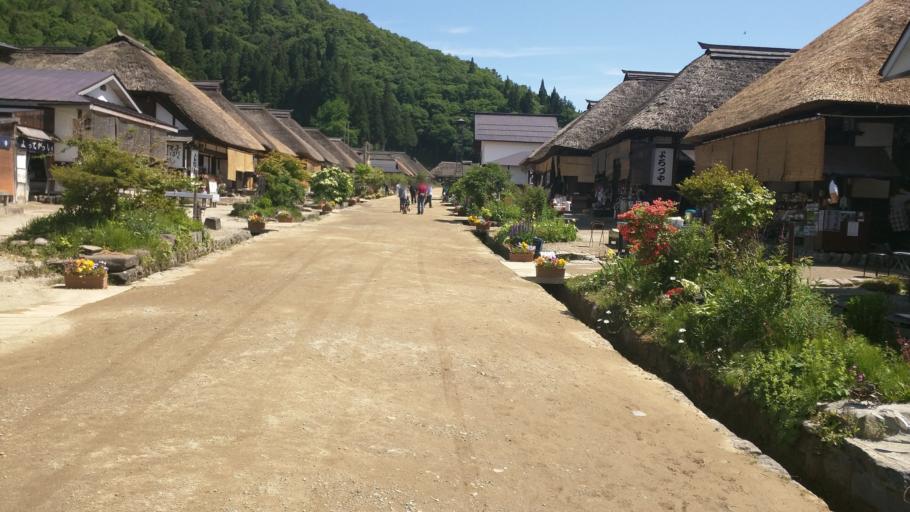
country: JP
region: Fukushima
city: Kitakata
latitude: 37.3328
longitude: 139.8604
